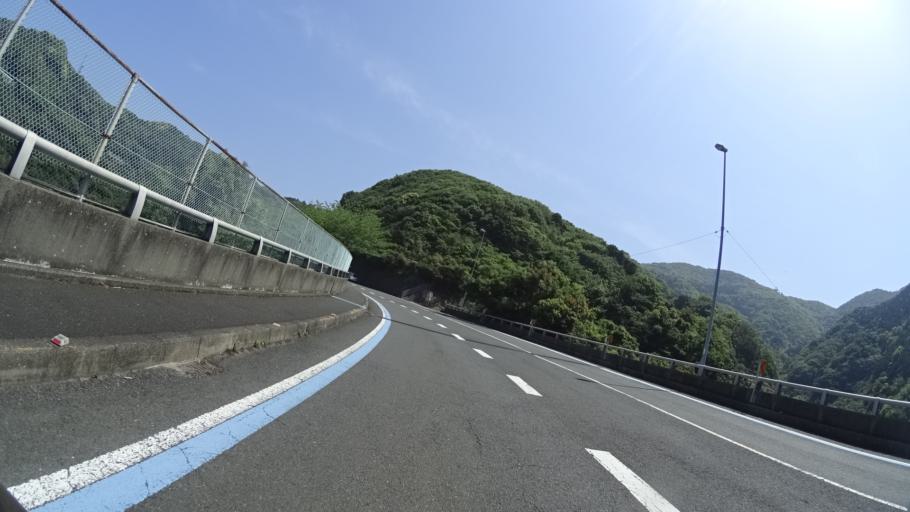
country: JP
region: Ehime
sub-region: Nishiuwa-gun
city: Ikata-cho
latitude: 33.3868
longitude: 132.1320
